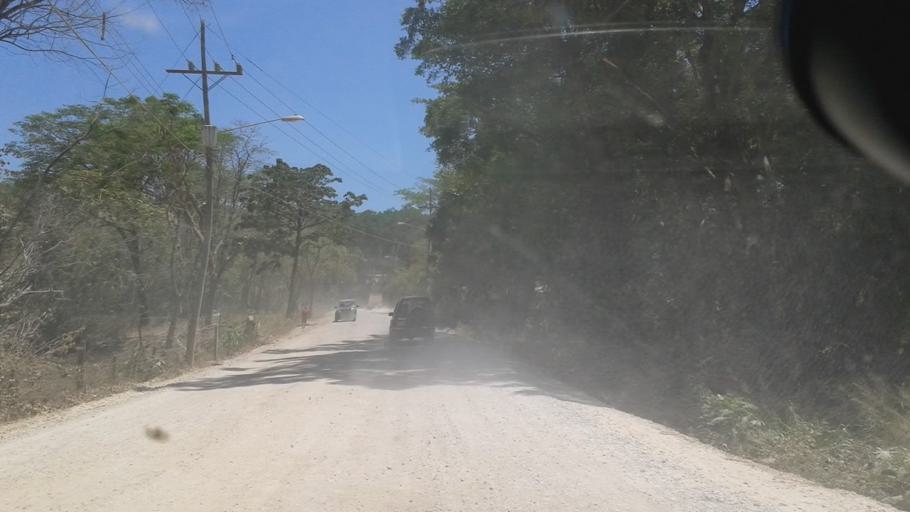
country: CR
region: Guanacaste
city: Samara
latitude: 9.9665
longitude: -85.6633
